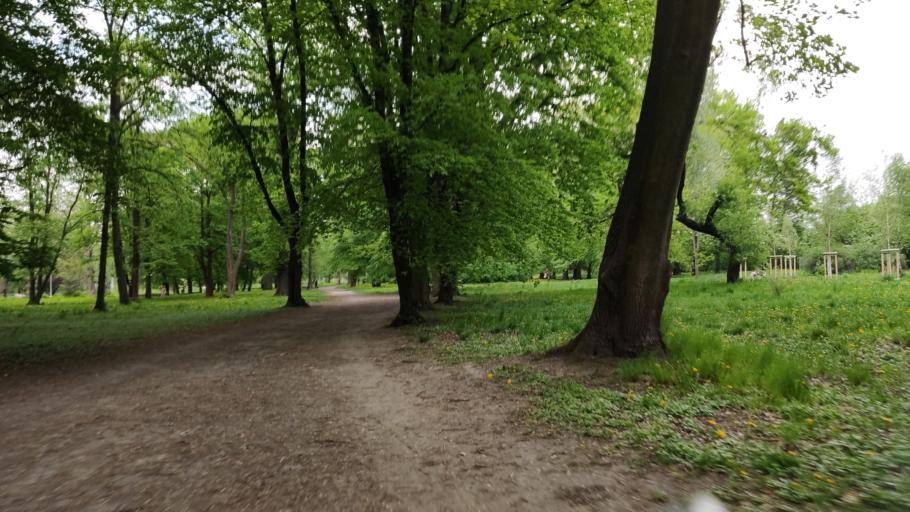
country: PL
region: Lower Silesian Voivodeship
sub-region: Powiat wroclawski
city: Wroclaw
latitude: 51.0778
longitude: 17.0267
